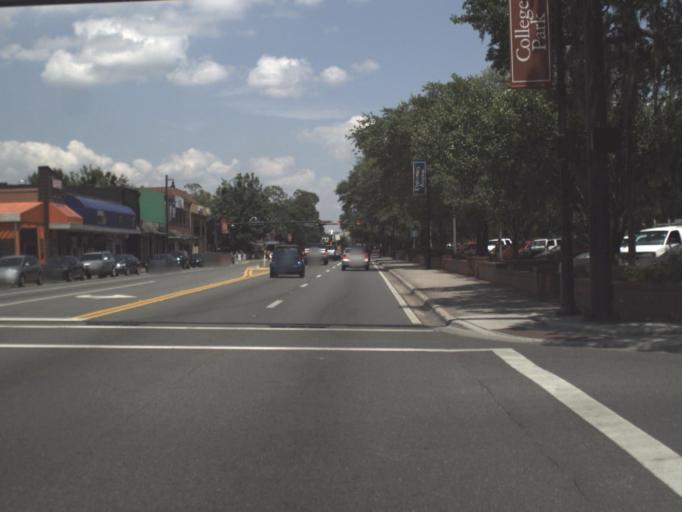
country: US
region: Florida
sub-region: Alachua County
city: Gainesville
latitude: 29.6520
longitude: -82.3464
